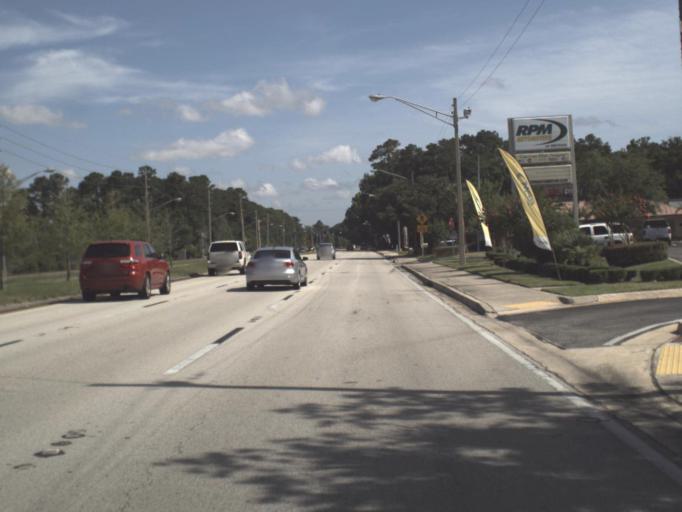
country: US
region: Florida
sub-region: Clay County
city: Bellair-Meadowbrook Terrace
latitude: 30.2508
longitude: -81.6984
